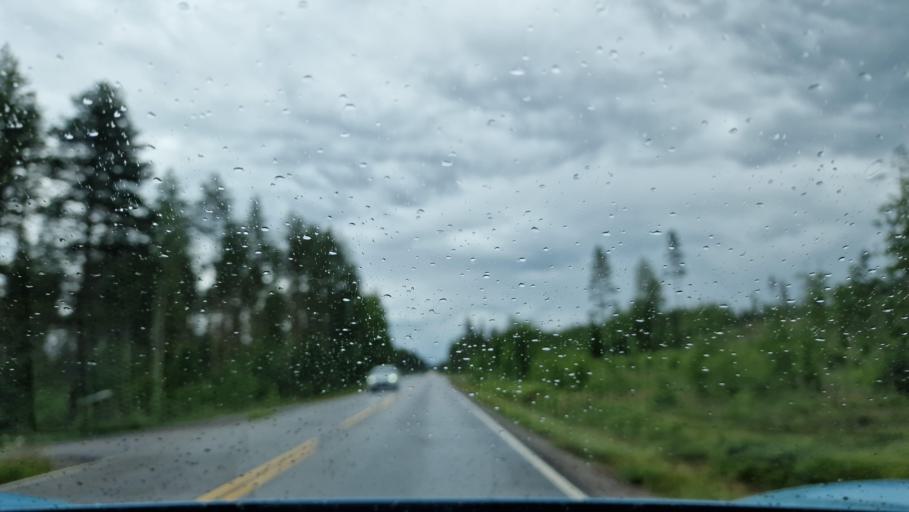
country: FI
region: Central Finland
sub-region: Saarijaervi-Viitasaari
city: Pylkoenmaeki
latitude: 62.6287
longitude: 24.5794
